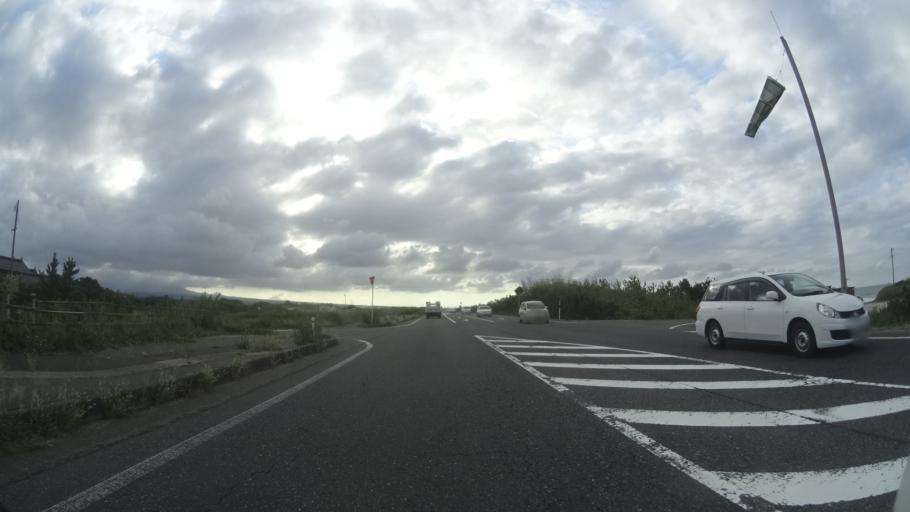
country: JP
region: Tottori
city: Kurayoshi
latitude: 35.5003
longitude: 133.7439
